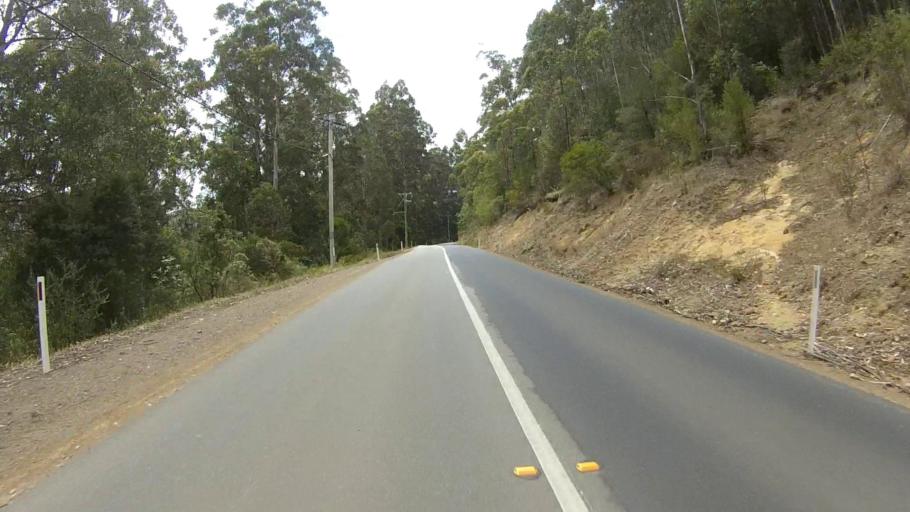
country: AU
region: Tasmania
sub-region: Huon Valley
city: Cygnet
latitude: -43.1307
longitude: 147.1577
